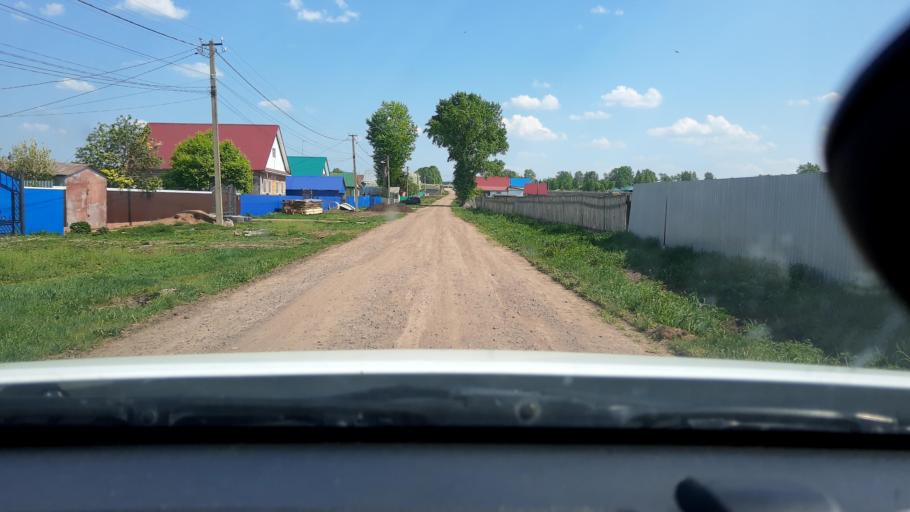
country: RU
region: Bashkortostan
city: Asanovo
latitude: 54.8449
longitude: 55.4541
